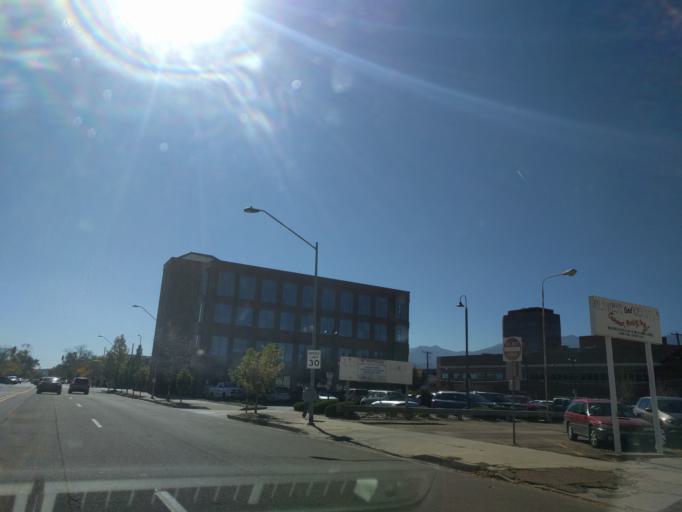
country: US
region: Colorado
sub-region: El Paso County
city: Colorado Springs
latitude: 38.8334
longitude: -104.8199
